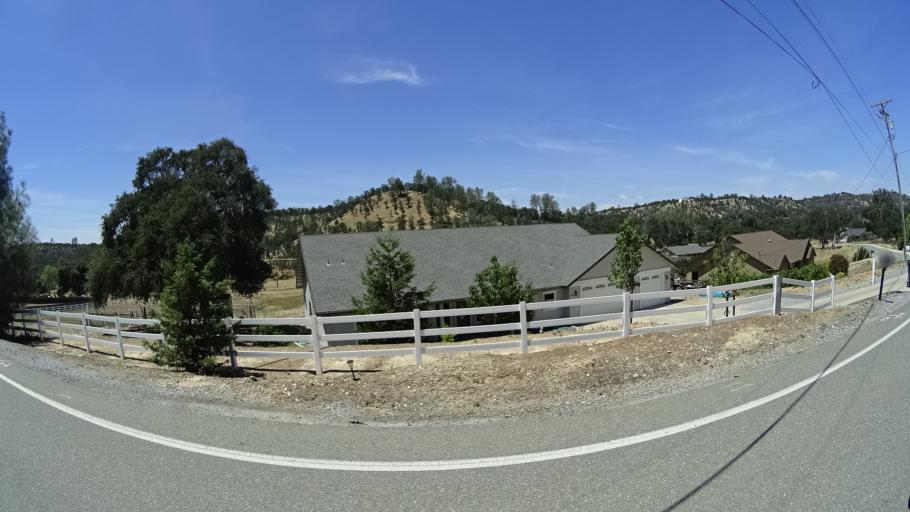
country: US
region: California
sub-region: Calaveras County
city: Rancho Calaveras
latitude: 38.1364
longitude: -120.8627
